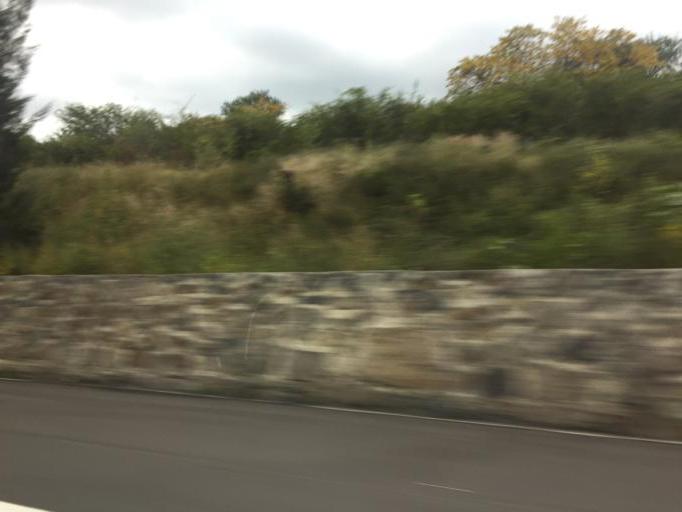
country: MX
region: Jalisco
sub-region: Poncitlan
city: Santa Cruz el Grande
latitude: 20.4431
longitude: -102.8307
